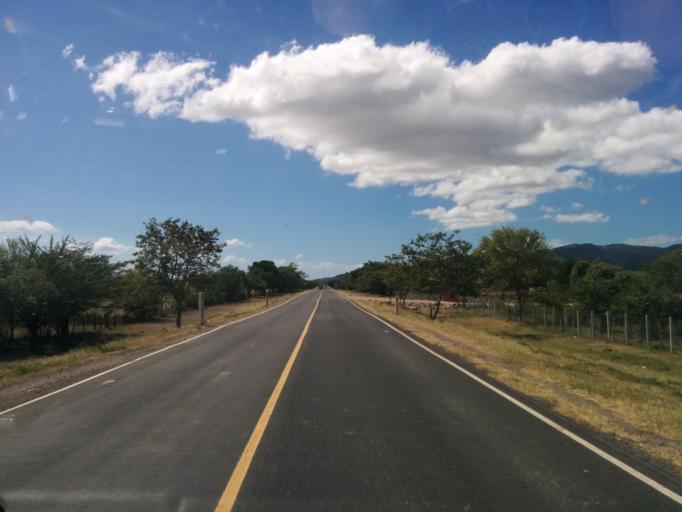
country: NI
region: Matagalpa
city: Ciudad Dario
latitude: 12.8676
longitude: -86.1974
